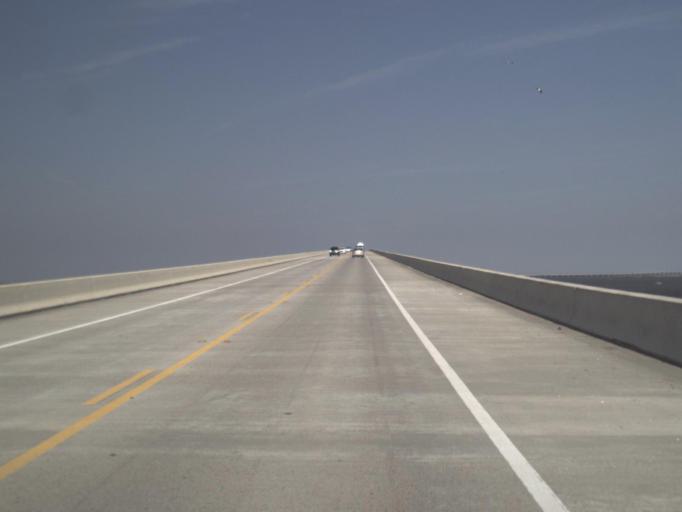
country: US
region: Florida
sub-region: Franklin County
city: Eastpoint
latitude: 29.6792
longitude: -84.8755
